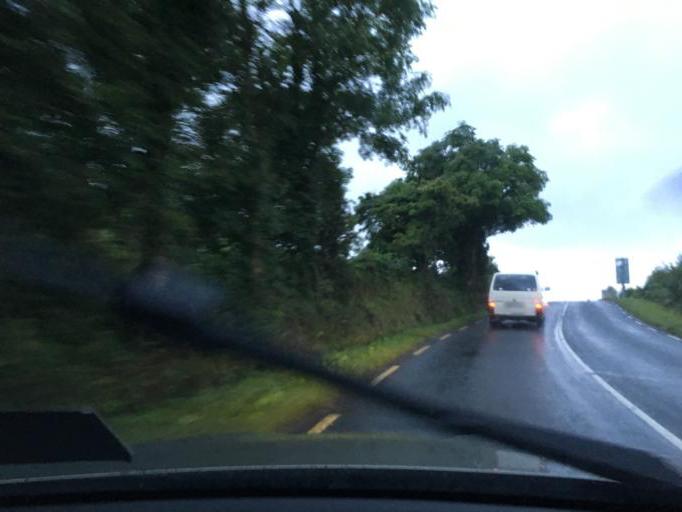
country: IE
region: Ulster
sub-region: County Donegal
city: Killybegs
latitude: 54.6374
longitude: -8.4754
